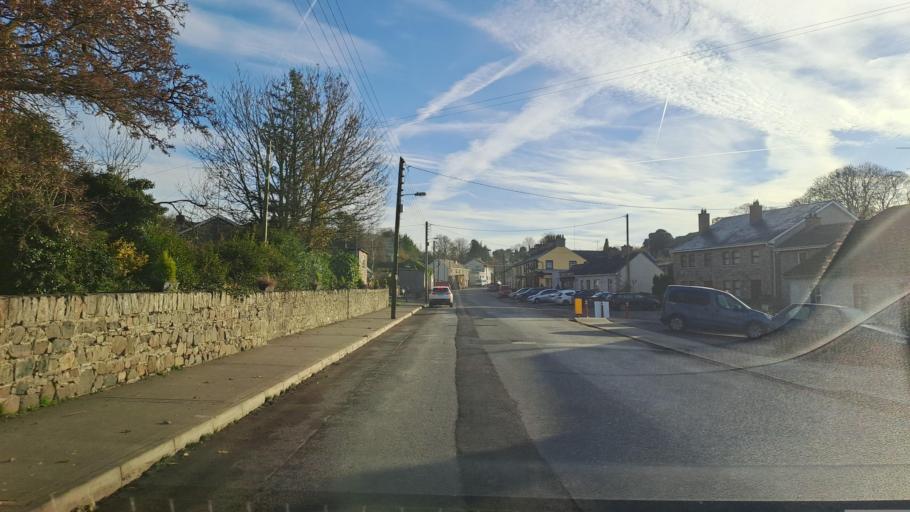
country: IE
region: Leinster
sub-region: Lu
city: Ardee
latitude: 53.8515
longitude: -6.6561
